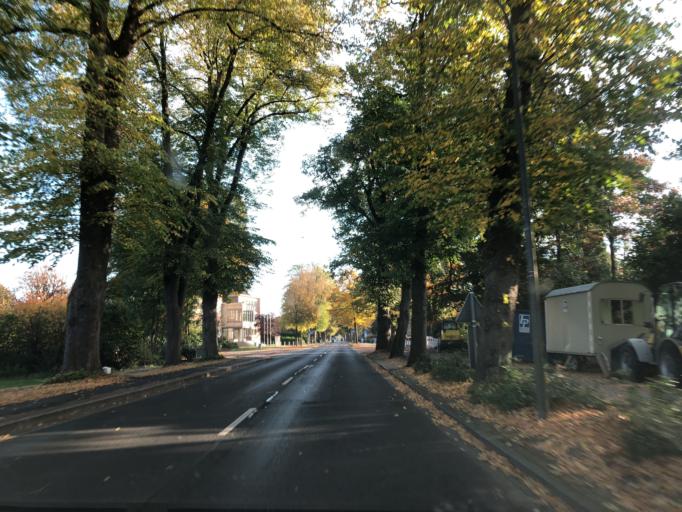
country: DE
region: Lower Saxony
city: Lehe
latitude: 53.0540
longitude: 7.3404
